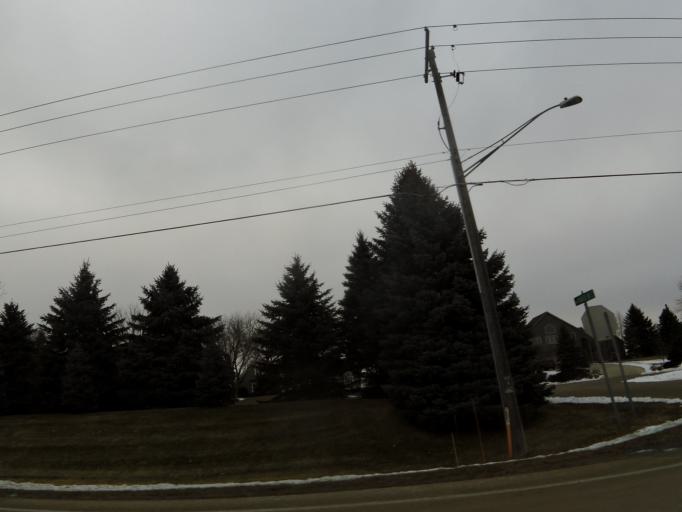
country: US
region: Minnesota
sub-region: Carver County
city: Waconia
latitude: 44.8551
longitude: -93.8049
